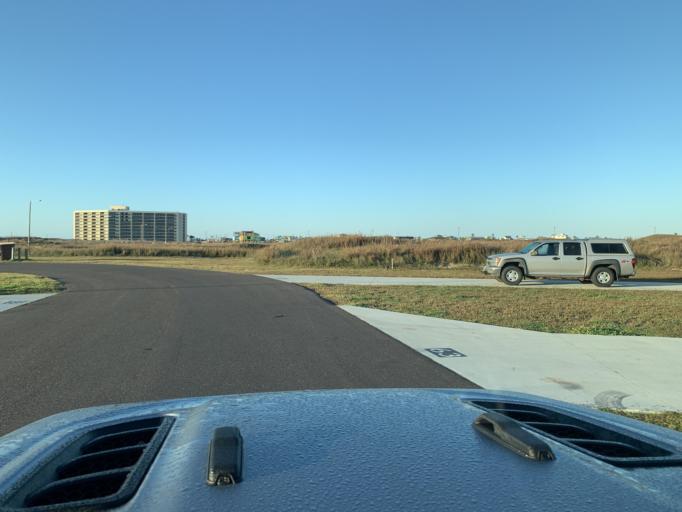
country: US
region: Texas
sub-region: Nueces County
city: Port Aransas
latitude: 27.8315
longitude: -97.0522
